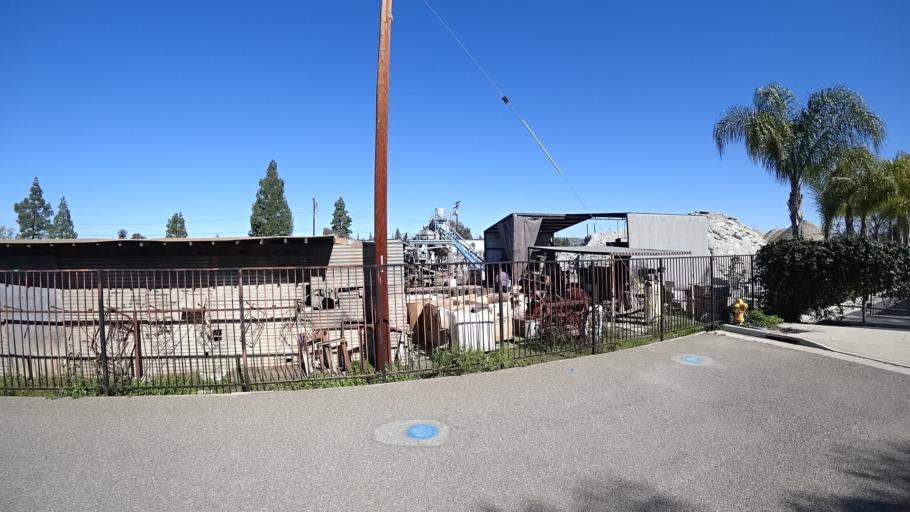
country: US
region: California
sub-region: Orange County
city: Yorba Linda
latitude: 33.8646
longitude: -117.8215
